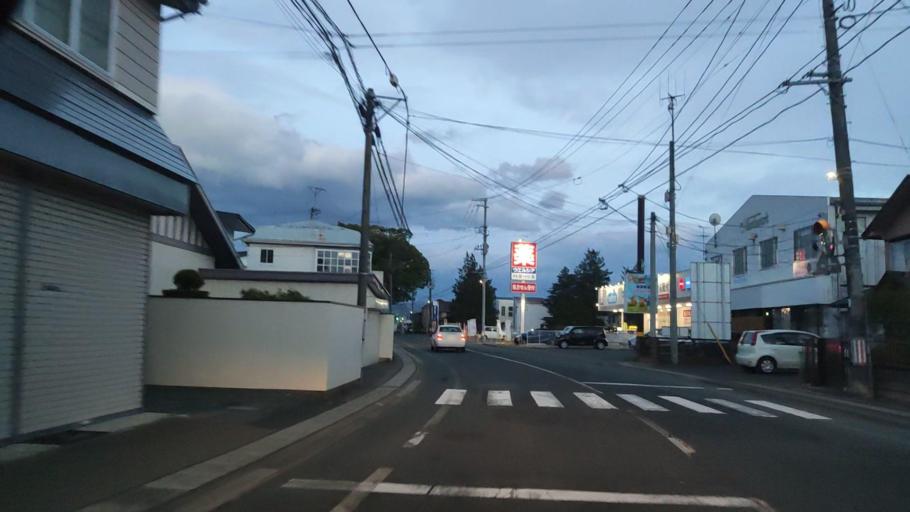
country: JP
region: Iwate
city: Morioka-shi
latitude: 39.7176
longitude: 141.1231
